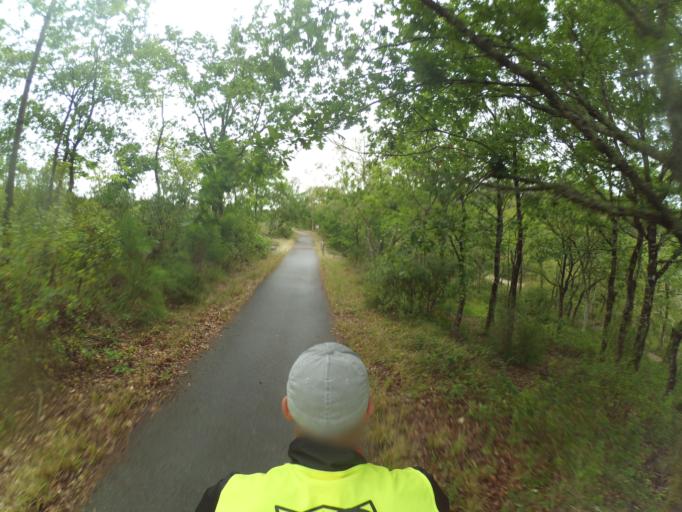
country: FR
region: Aquitaine
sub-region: Departement des Landes
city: Mimizan
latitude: 44.2196
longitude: -1.2402
